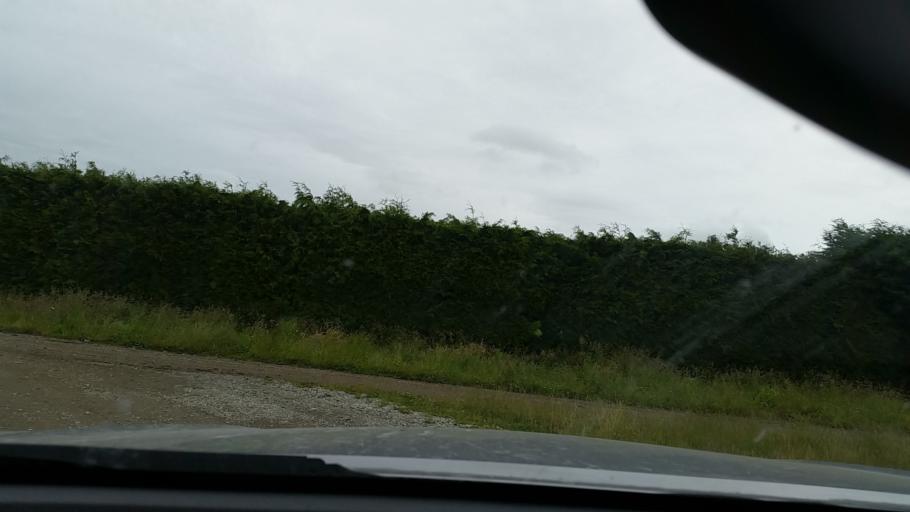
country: NZ
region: Southland
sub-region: Southland District
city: Winton
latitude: -46.1319
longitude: 168.2812
